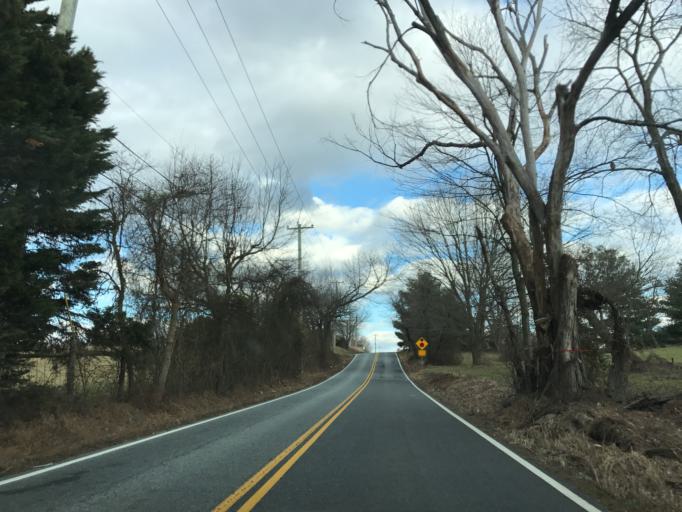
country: US
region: Maryland
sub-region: Cecil County
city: Rising Sun
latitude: 39.6371
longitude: -76.0244
